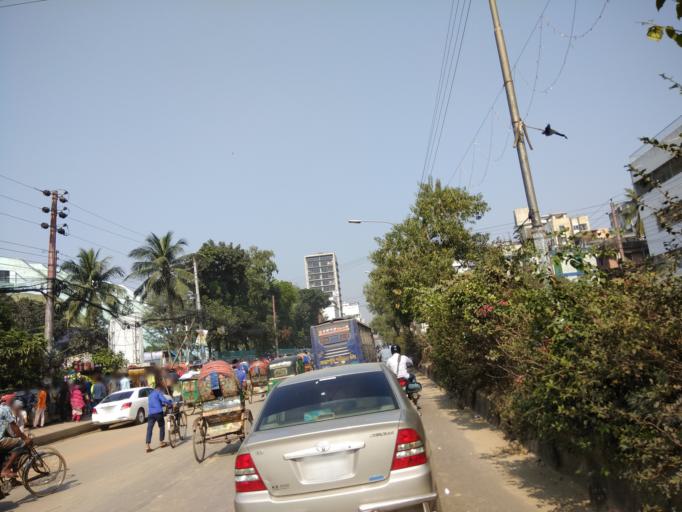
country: BD
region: Dhaka
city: Azimpur
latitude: 23.8108
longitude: 90.3675
